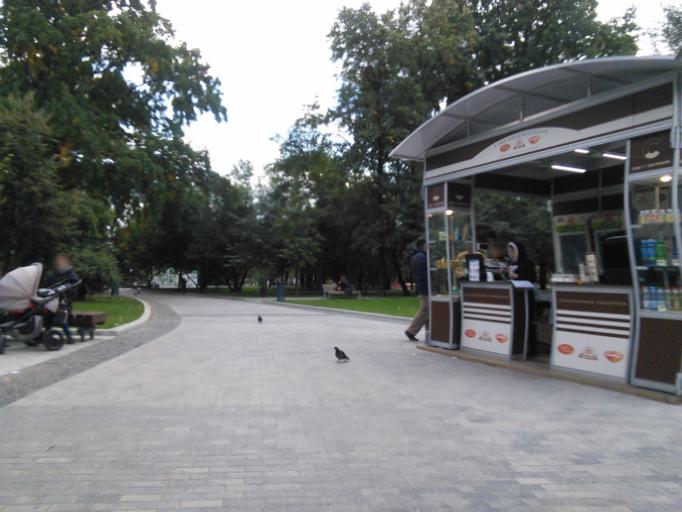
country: RU
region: Moscow
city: Taganskiy
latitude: 55.7675
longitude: 37.6597
